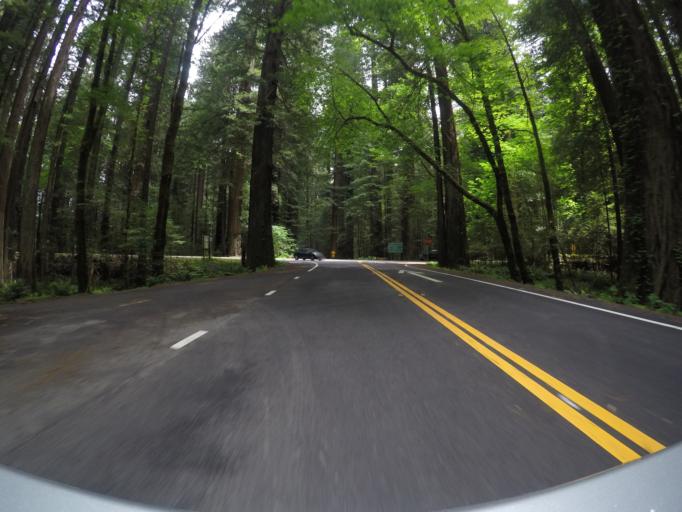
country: US
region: California
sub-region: Humboldt County
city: Rio Dell
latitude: 40.3526
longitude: -123.9266
